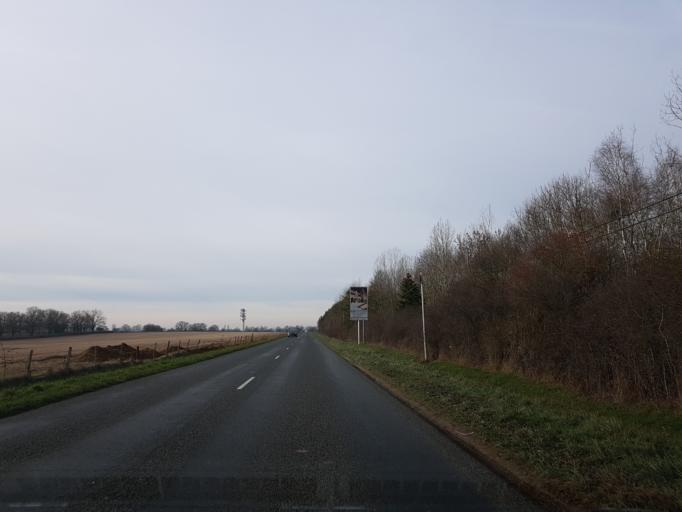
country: FR
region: Auvergne
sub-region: Departement de l'Allier
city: Yzeure
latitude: 46.5786
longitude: 3.4000
